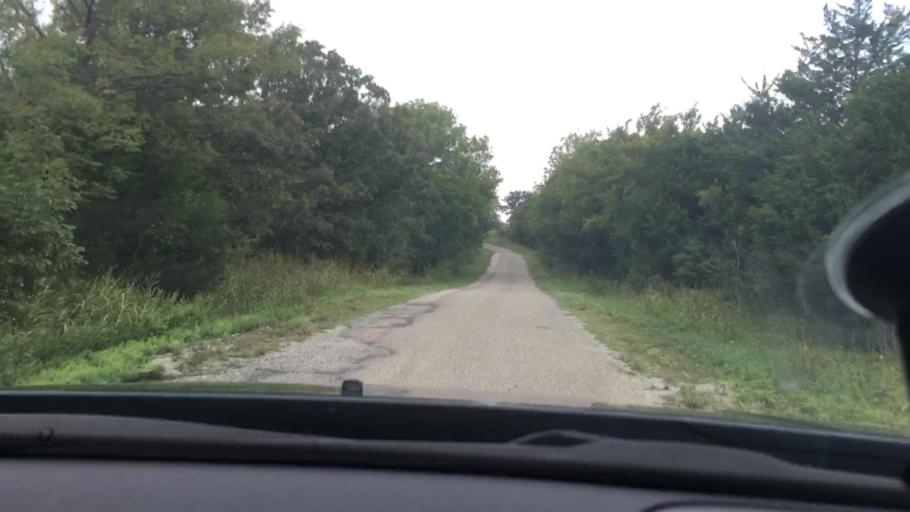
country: US
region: Oklahoma
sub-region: Pontotoc County
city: Byng
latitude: 34.8182
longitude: -96.5358
